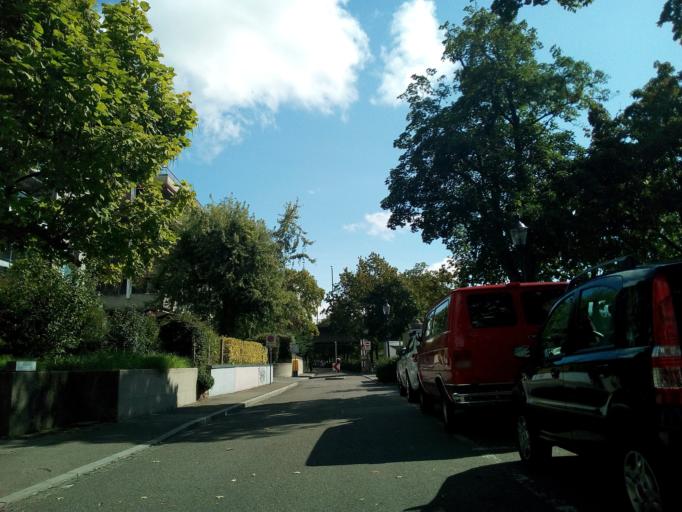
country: CH
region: Basel-City
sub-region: Basel-Stadt
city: Basel
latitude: 47.5665
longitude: 7.5868
